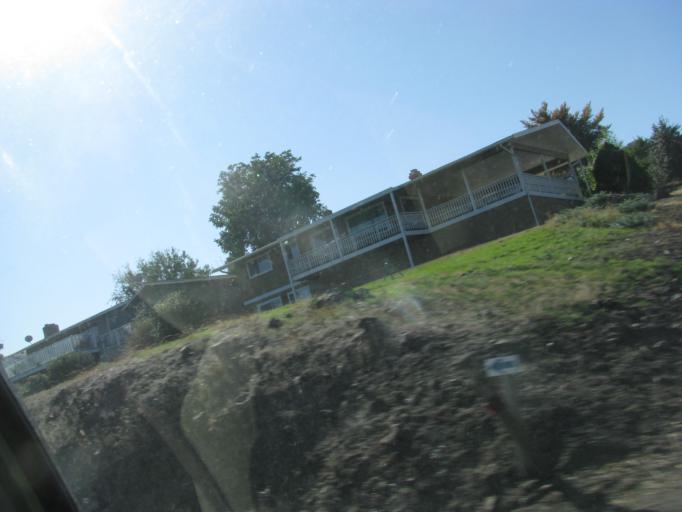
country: US
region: Washington
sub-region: Asotin County
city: Asotin
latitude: 46.3585
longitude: -117.0647
